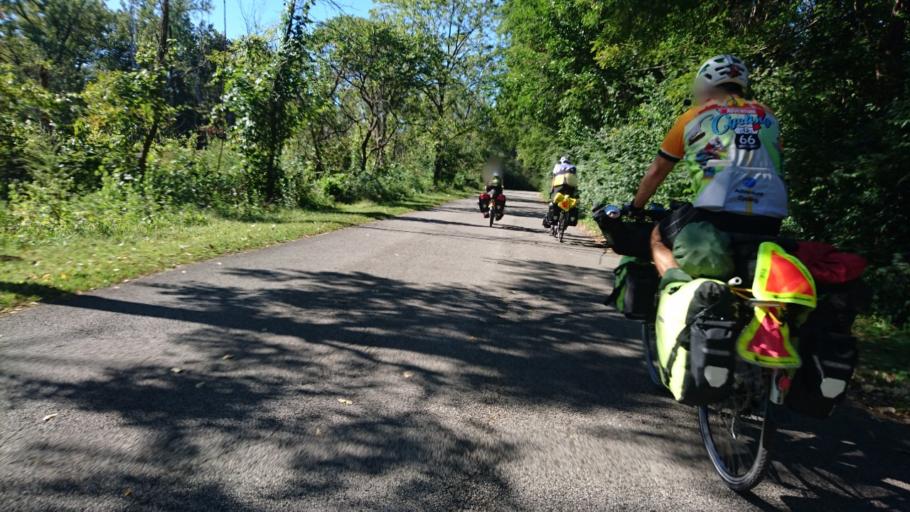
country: US
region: Illinois
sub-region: Cook County
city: Burnham
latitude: 41.6742
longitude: -87.5362
